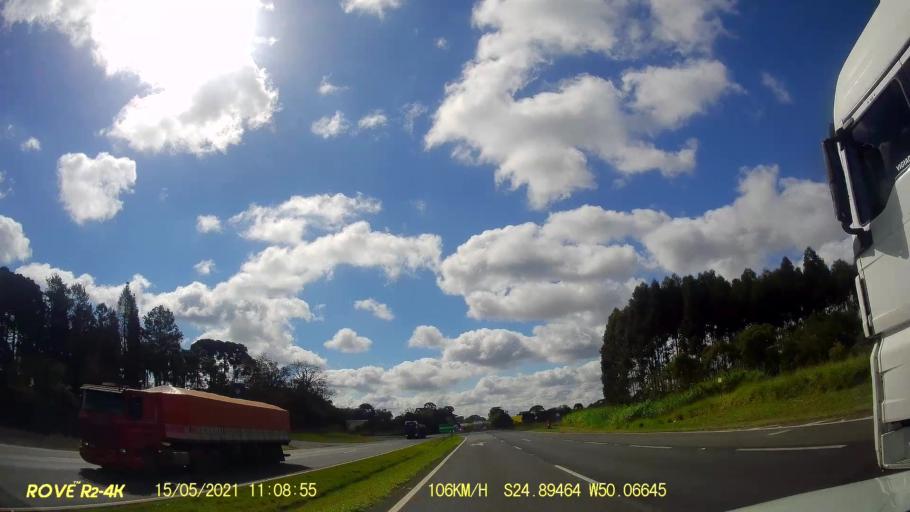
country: BR
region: Parana
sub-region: Carambei
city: Carambei
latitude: -24.8947
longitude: -50.0667
